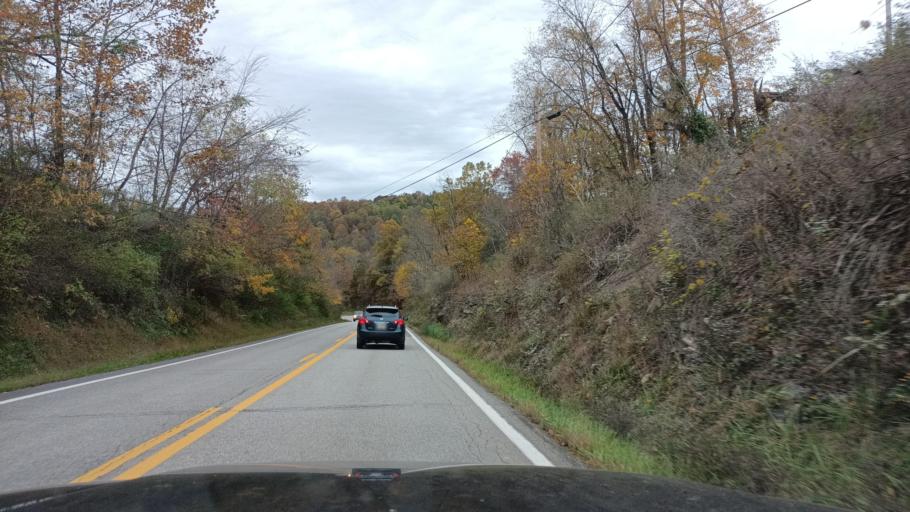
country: US
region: West Virginia
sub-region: Taylor County
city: Grafton
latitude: 39.3432
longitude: -79.9637
